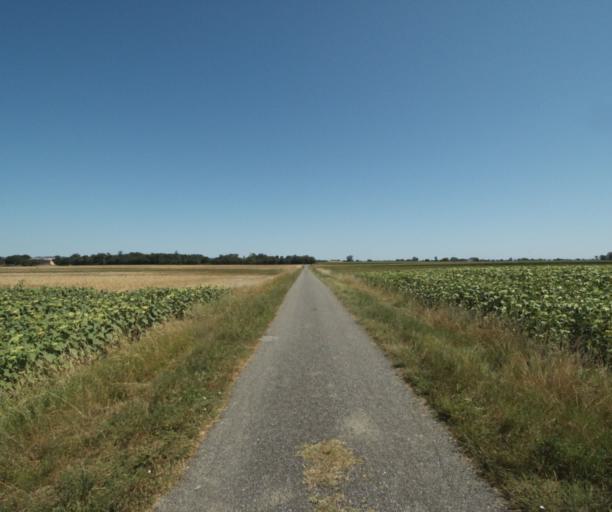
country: FR
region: Midi-Pyrenees
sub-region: Departement de la Haute-Garonne
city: Revel
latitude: 43.4746
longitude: 1.9656
